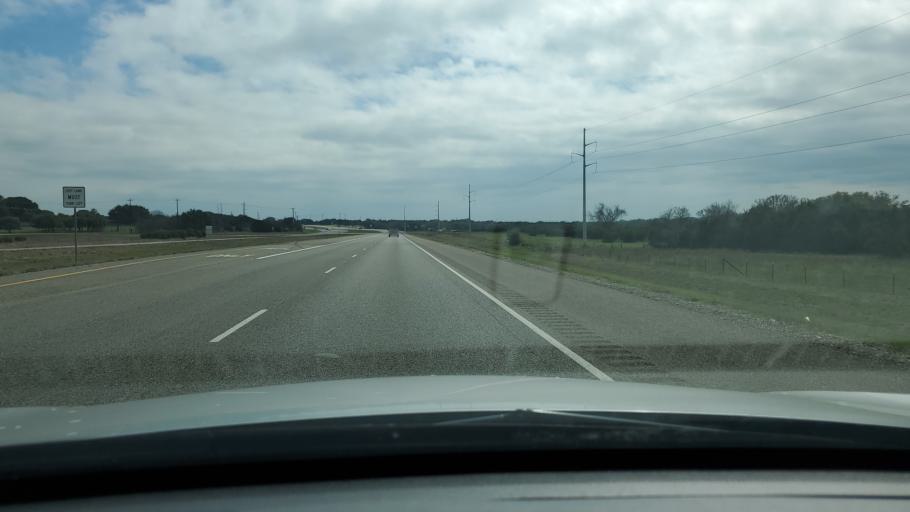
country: US
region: Texas
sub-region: Williamson County
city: Florence
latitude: 30.7658
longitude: -97.7503
